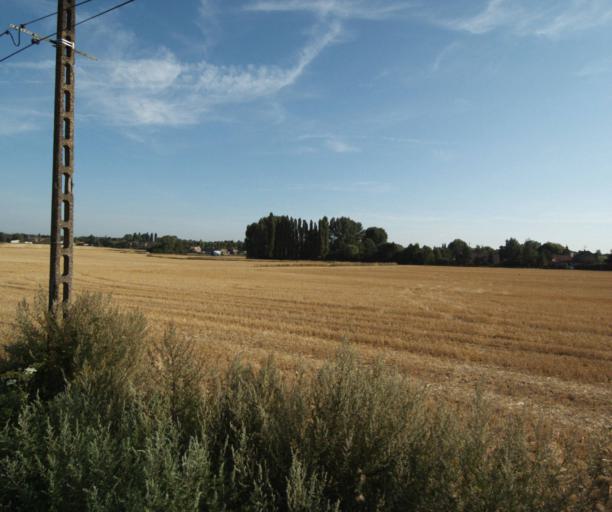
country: FR
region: Nord-Pas-de-Calais
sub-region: Departement du Nord
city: Roncq
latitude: 50.7658
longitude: 3.1401
